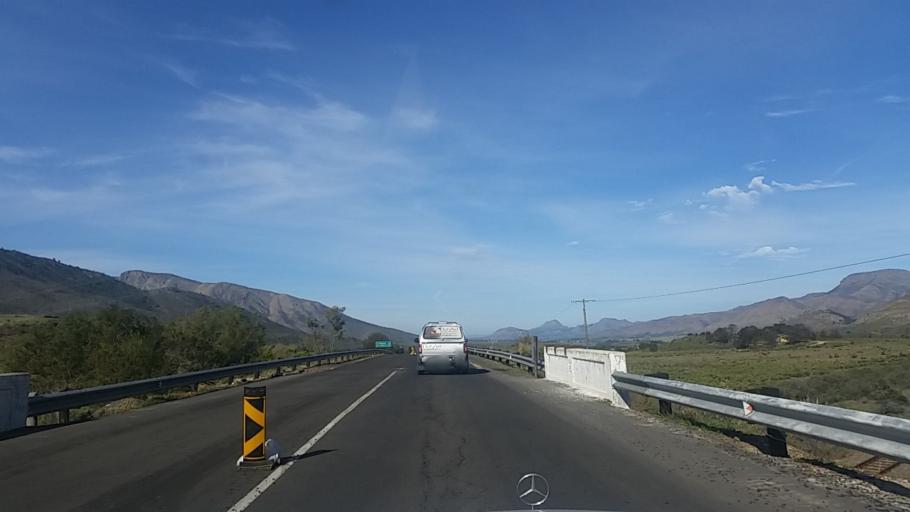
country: ZA
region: Western Cape
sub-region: Eden District Municipality
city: George
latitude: -33.8275
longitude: 22.4042
